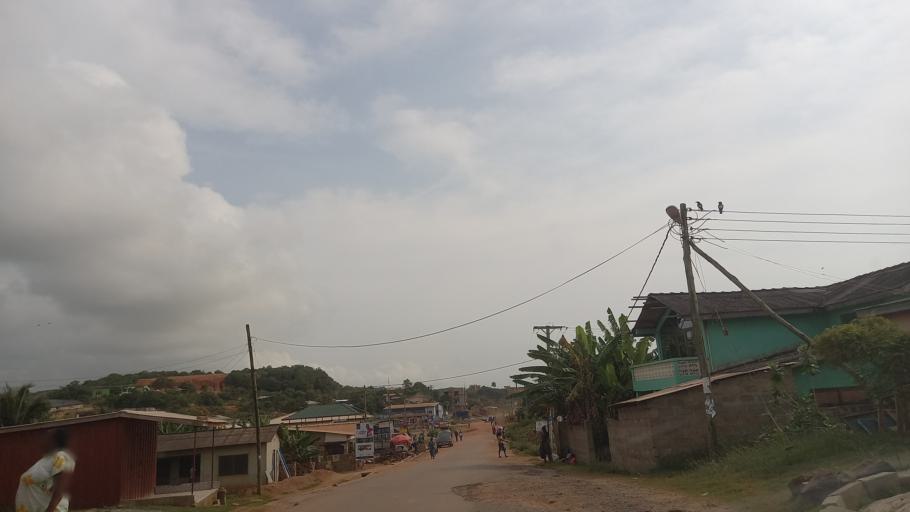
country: GH
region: Western
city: Shama Junction
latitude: 4.9751
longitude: -1.6492
